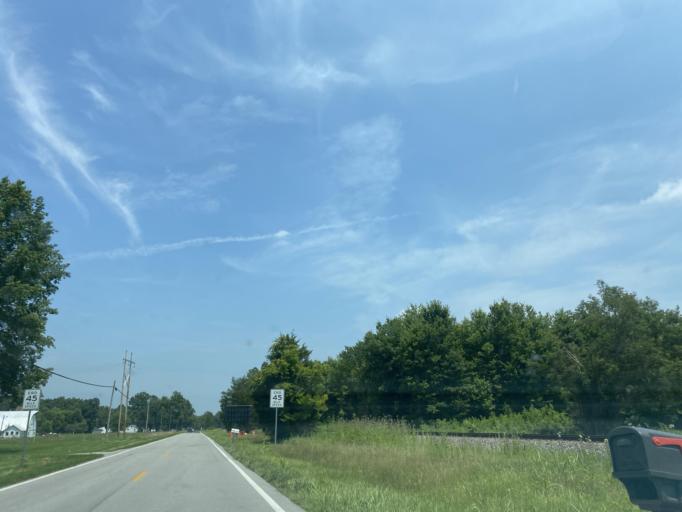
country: US
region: Kentucky
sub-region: Campbell County
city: Claryville
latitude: 38.8717
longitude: -84.4540
